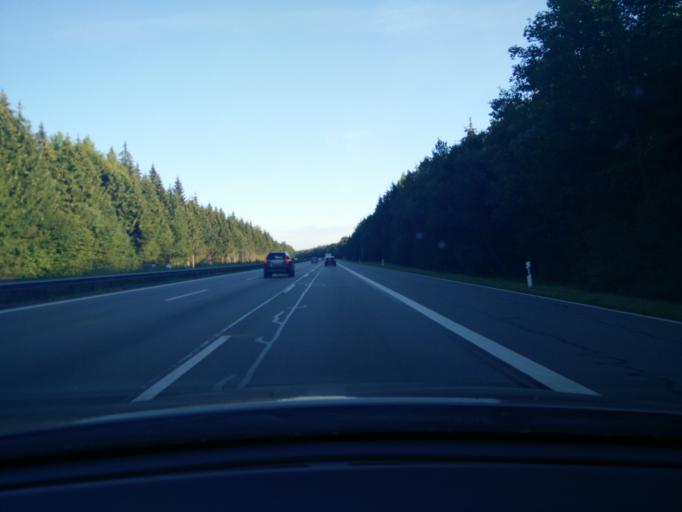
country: DE
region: Bavaria
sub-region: Upper Bavaria
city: Otterfing
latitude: 47.9232
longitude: 11.7118
